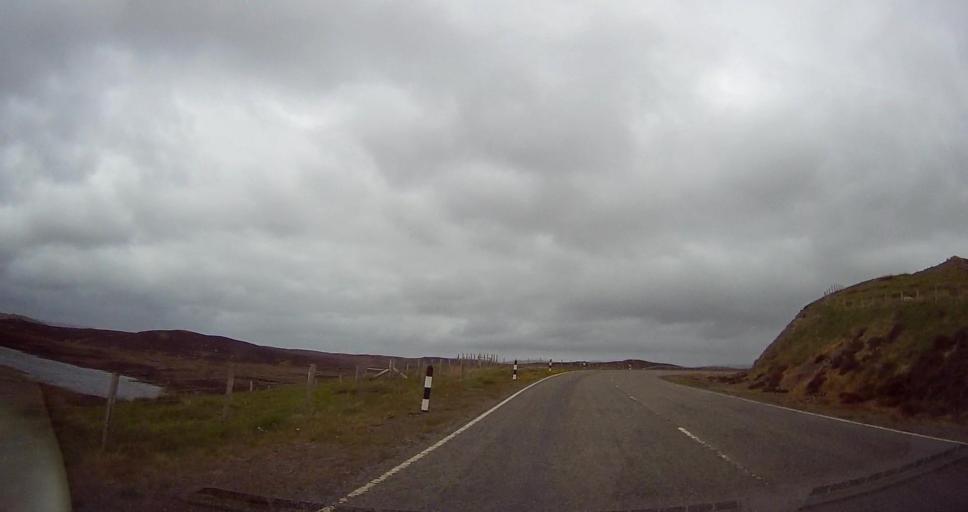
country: GB
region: Scotland
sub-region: Shetland Islands
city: Sandwick
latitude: 60.2587
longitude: -1.4865
